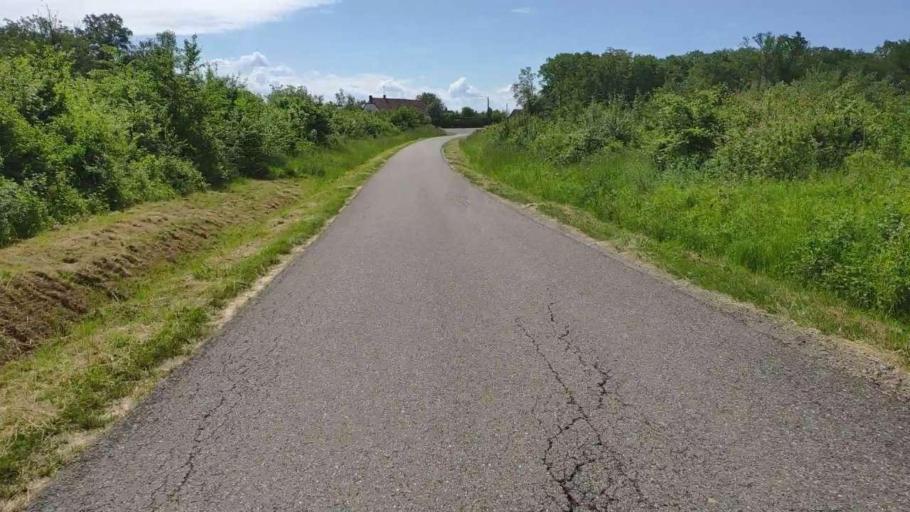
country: FR
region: Franche-Comte
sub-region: Departement du Jura
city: Bletterans
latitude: 46.7083
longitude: 5.4096
